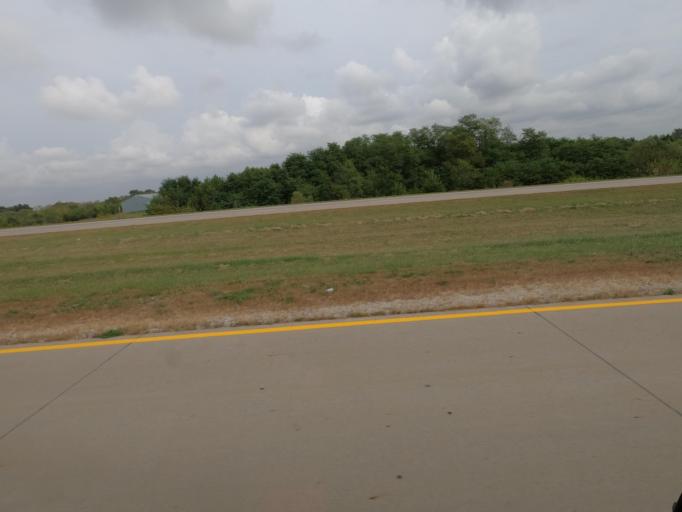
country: US
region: Iowa
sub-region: Wapello County
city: Ottumwa
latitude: 41.0728
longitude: -92.3940
